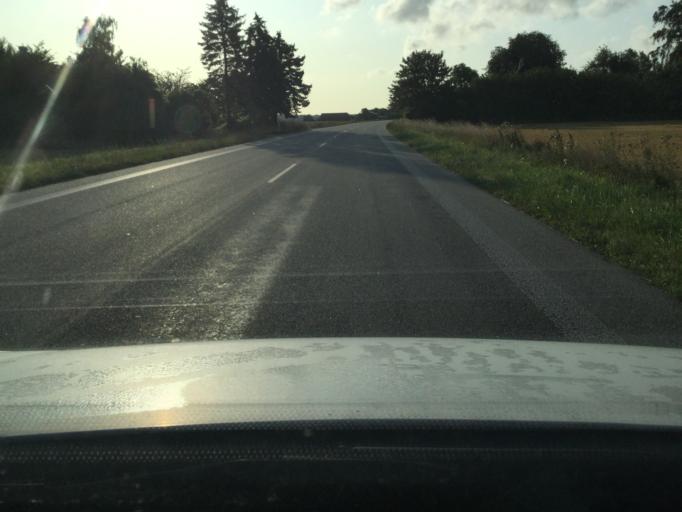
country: DK
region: Zealand
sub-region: Lolland Kommune
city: Rodby
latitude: 54.7646
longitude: 11.3140
